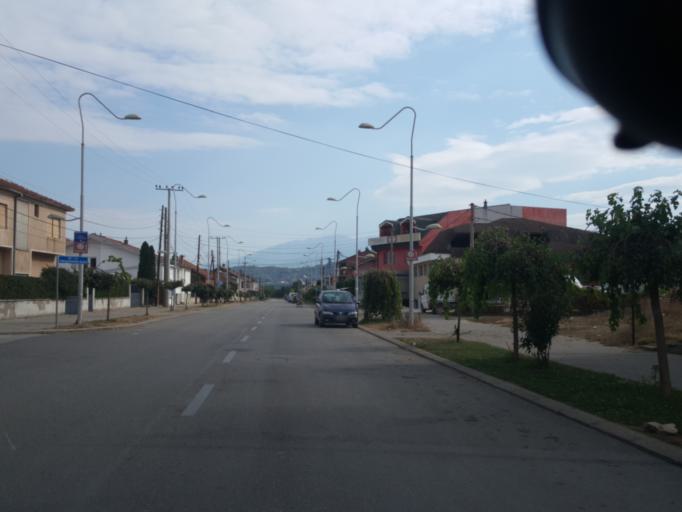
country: XK
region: Gjakova
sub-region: Komuna e Gjakoves
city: Gjakove
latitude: 42.3691
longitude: 20.4311
